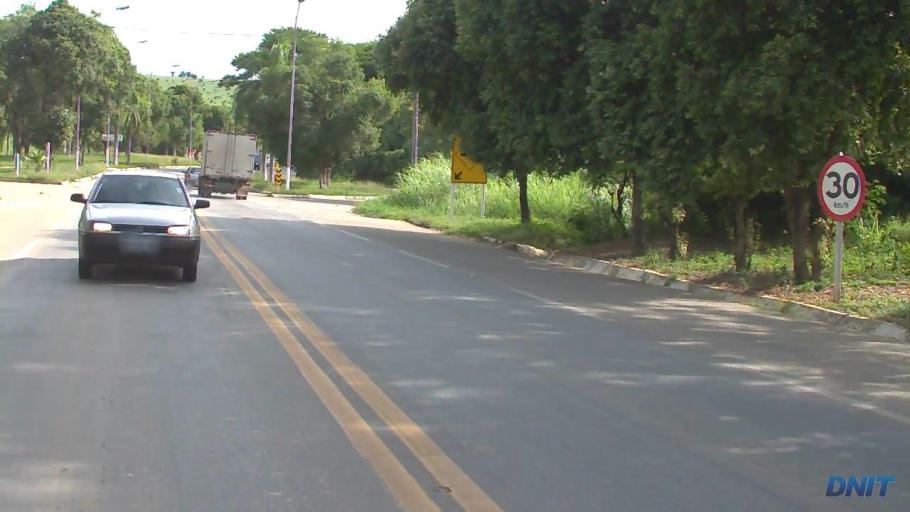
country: BR
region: Minas Gerais
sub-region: Belo Oriente
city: Belo Oriente
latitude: -19.2319
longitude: -42.3282
